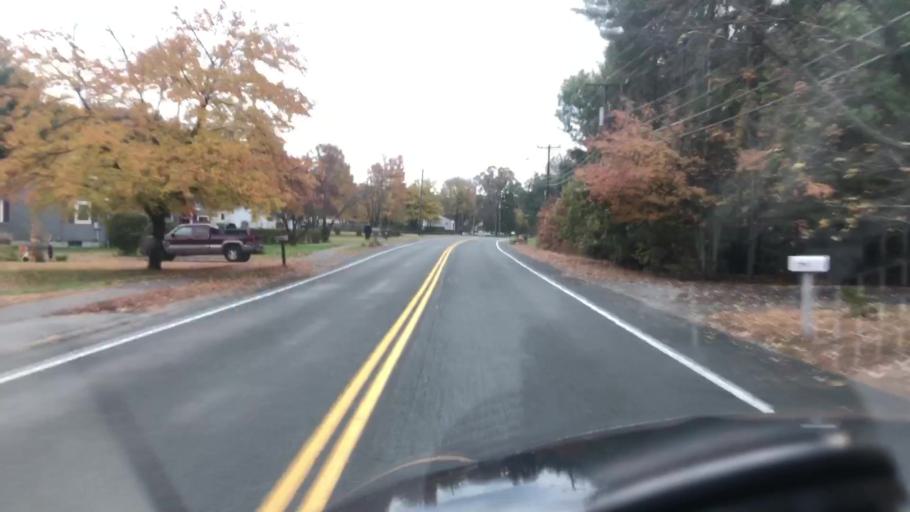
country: US
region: Massachusetts
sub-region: Hampshire County
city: Easthampton
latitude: 42.2412
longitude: -72.6852
